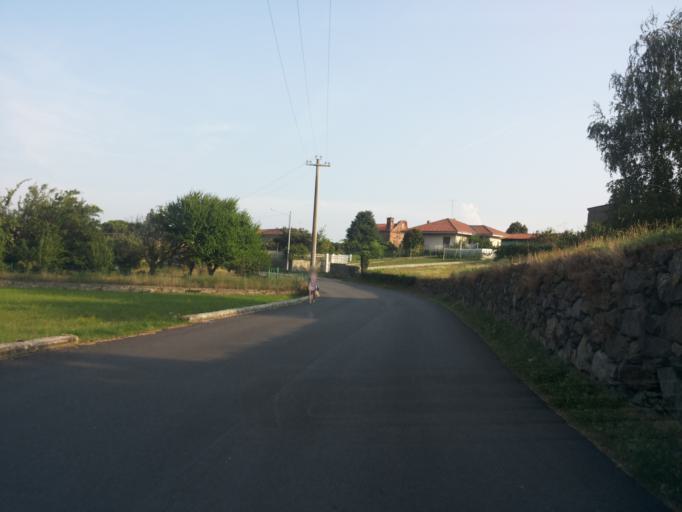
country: IT
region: Piedmont
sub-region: Provincia di Biella
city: Viverone
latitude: 45.4258
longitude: 8.0563
